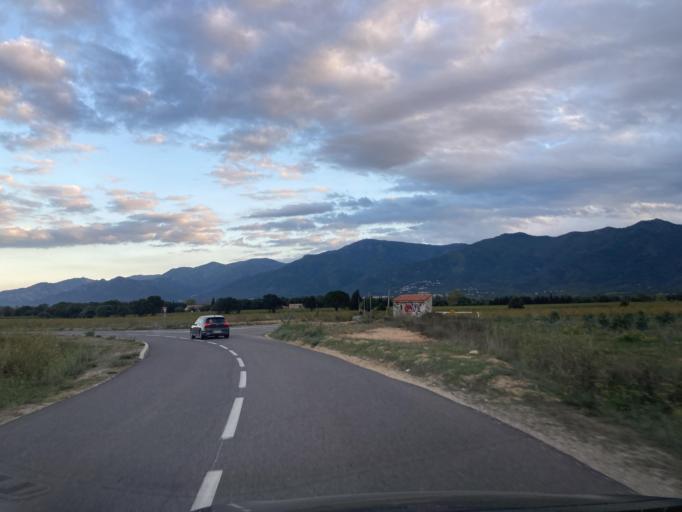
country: FR
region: Languedoc-Roussillon
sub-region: Departement des Pyrenees-Orientales
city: Banyuls-dels-Aspres
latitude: 42.5606
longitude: 2.8808
